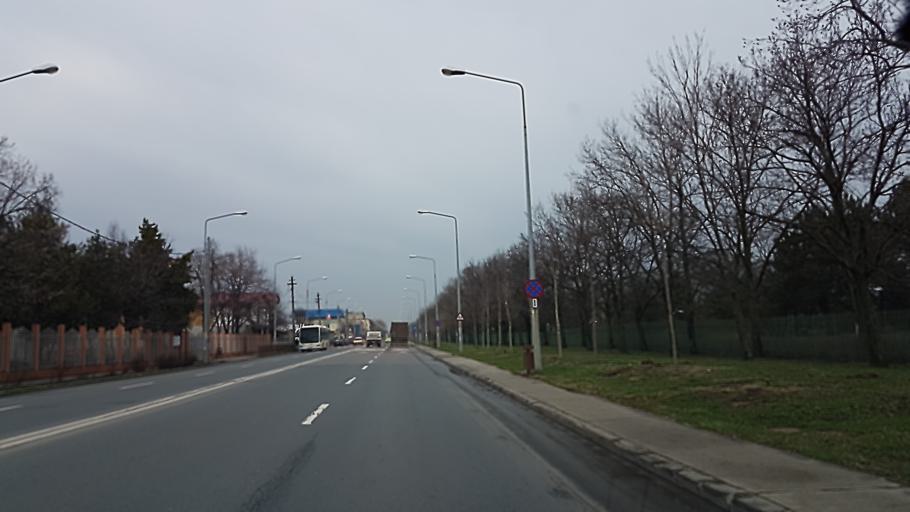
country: RO
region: Ilfov
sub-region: Comuna Pantelimon
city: Pantelimon
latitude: 44.4357
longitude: 26.2021
